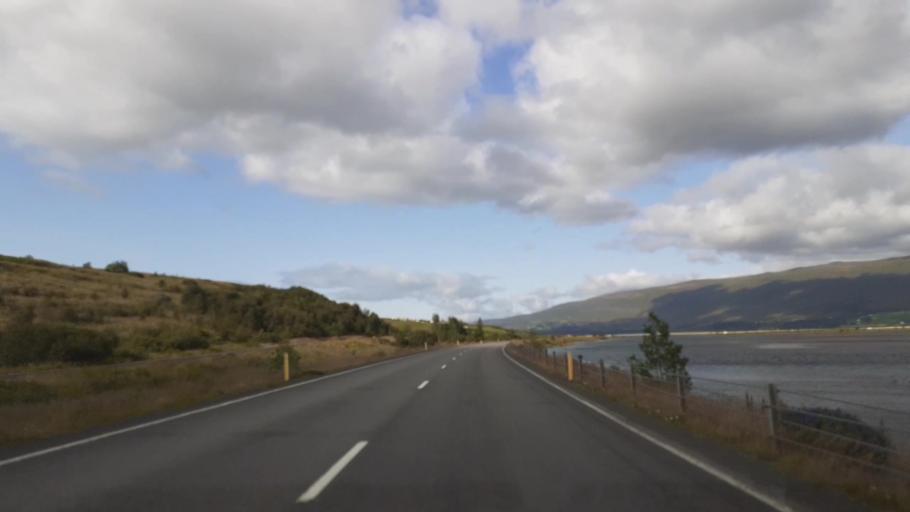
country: IS
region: Northeast
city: Akureyri
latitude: 65.6121
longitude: -18.0797
